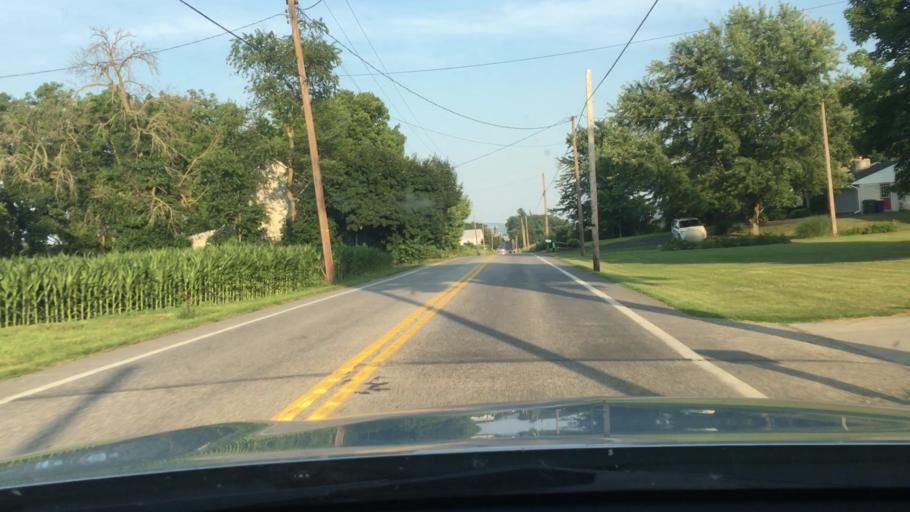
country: US
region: Pennsylvania
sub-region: Cumberland County
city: Boiling Springs
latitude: 40.1688
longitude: -77.1122
